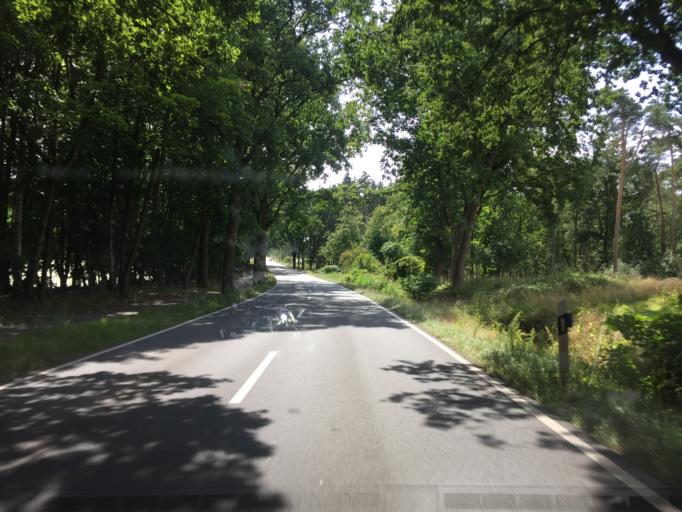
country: DE
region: Lower Saxony
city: Bohme
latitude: 52.8159
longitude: 9.4444
